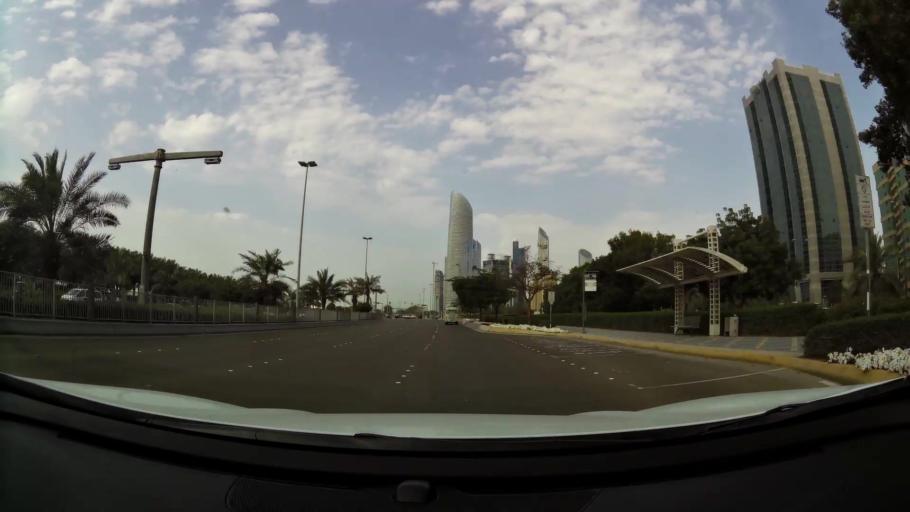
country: AE
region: Abu Dhabi
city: Abu Dhabi
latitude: 24.4762
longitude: 54.3445
